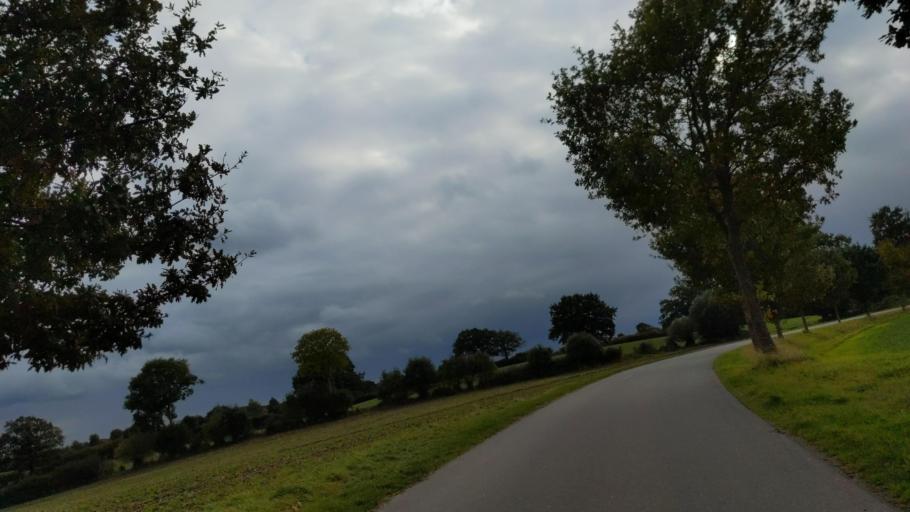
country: DE
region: Schleswig-Holstein
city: Sierksdorf
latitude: 54.0975
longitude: 10.7642
